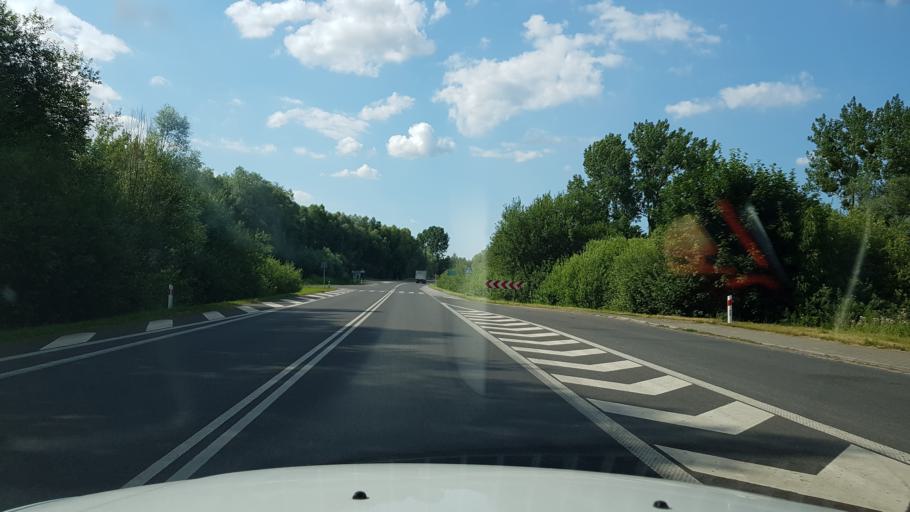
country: PL
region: West Pomeranian Voivodeship
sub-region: Powiat gryfinski
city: Stare Czarnowo
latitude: 53.2393
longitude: 14.7850
